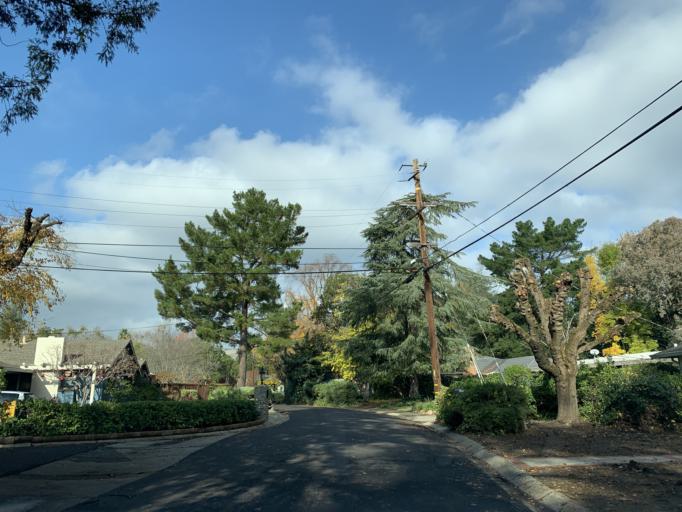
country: US
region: California
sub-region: Contra Costa County
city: Saranap
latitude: 37.8906
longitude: -122.0660
